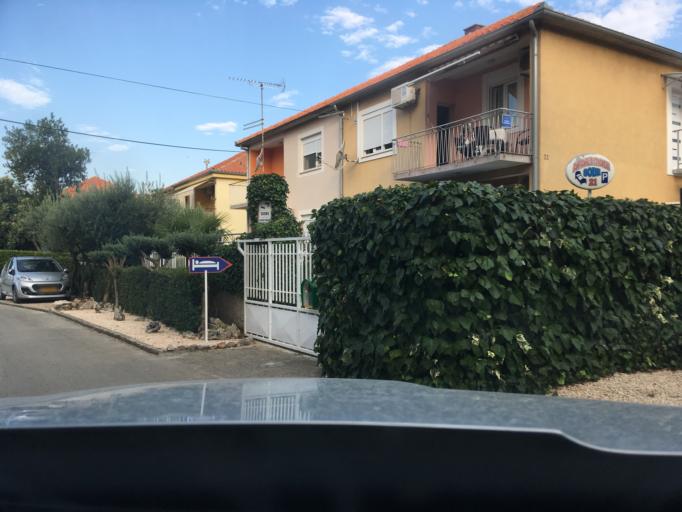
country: HR
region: Zadarska
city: Zadar
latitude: 44.1281
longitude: 15.2241
